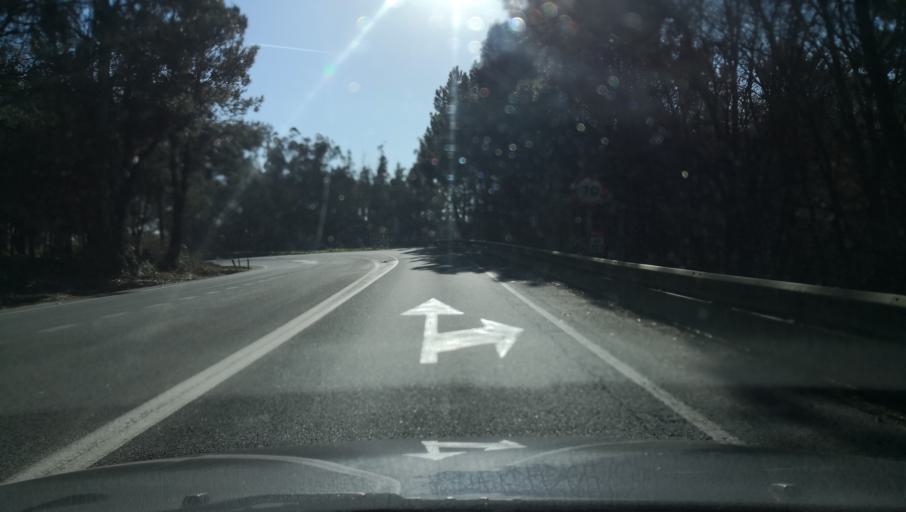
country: ES
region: Galicia
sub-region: Provincia da Coruna
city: Vedra
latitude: 42.7912
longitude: -8.4586
